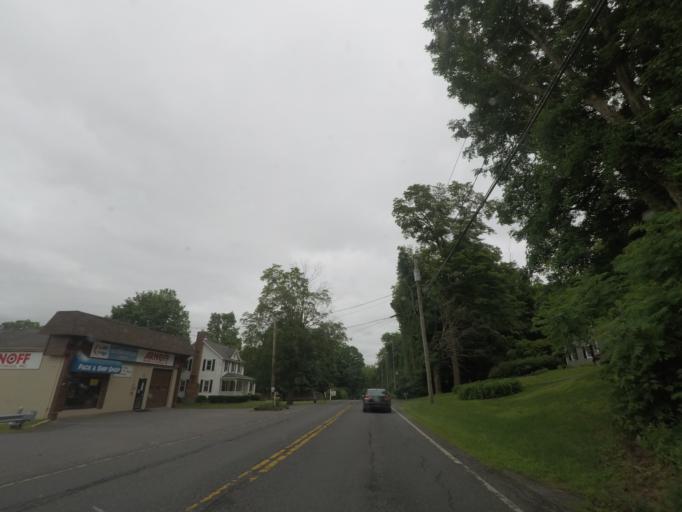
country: US
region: Connecticut
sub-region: Litchfield County
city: Canaan
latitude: 41.9553
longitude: -73.4767
